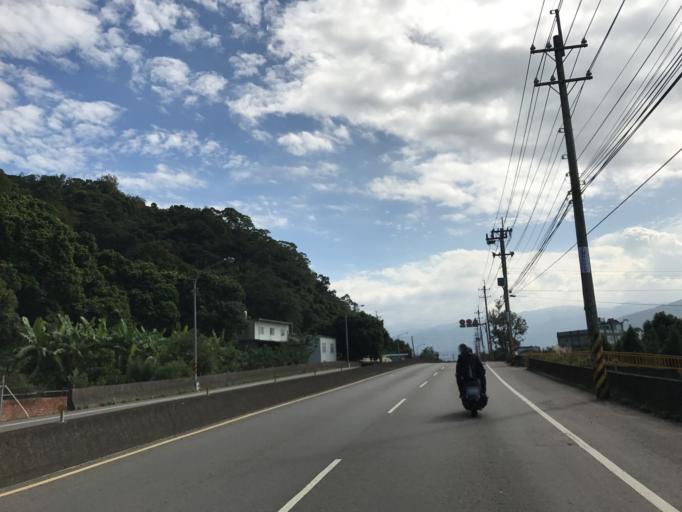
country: TW
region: Taiwan
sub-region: Hsinchu
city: Zhubei
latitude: 24.7403
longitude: 121.1101
